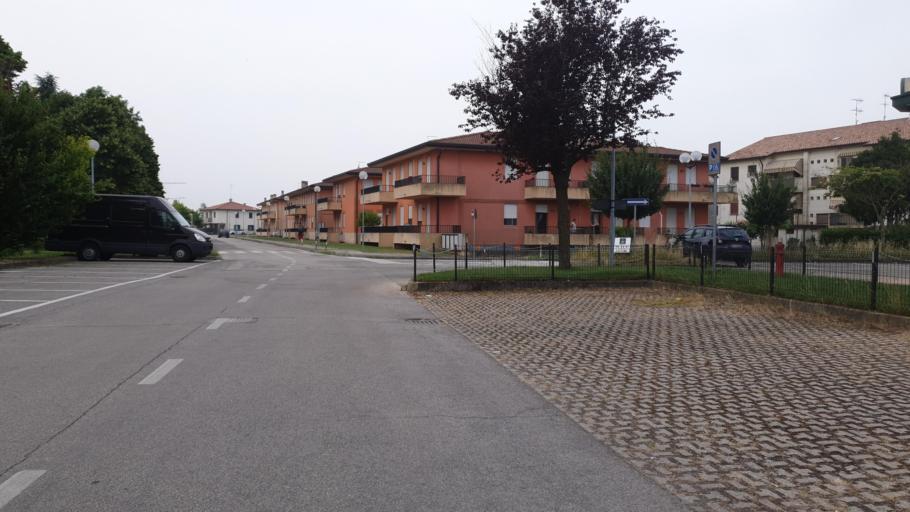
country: IT
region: Veneto
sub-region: Provincia di Padova
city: Piove di Sacco-Piovega
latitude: 45.2885
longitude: 12.0293
